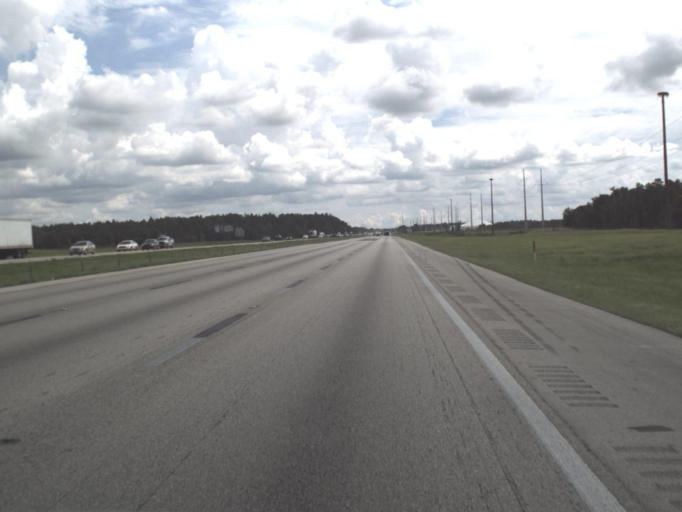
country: US
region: Florida
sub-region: Polk County
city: Polk City
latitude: 28.1457
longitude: -81.8777
